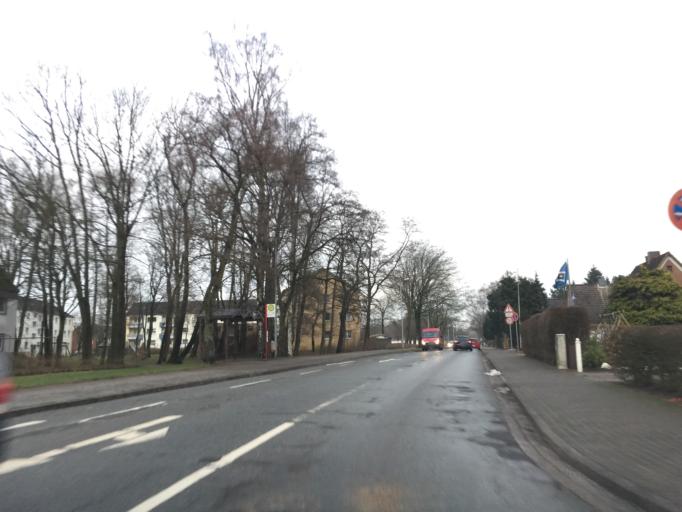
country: DE
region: Schleswig-Holstein
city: Wahlstedt
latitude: 53.9502
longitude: 10.2013
